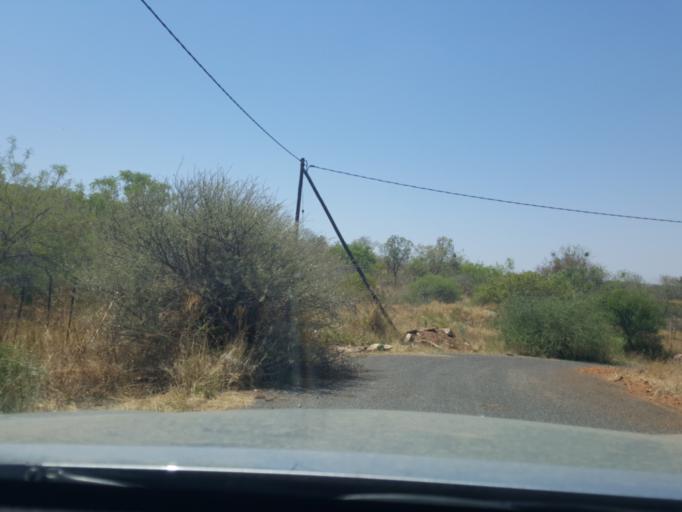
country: BW
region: South East
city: Lobatse
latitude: -25.1859
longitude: 25.6777
